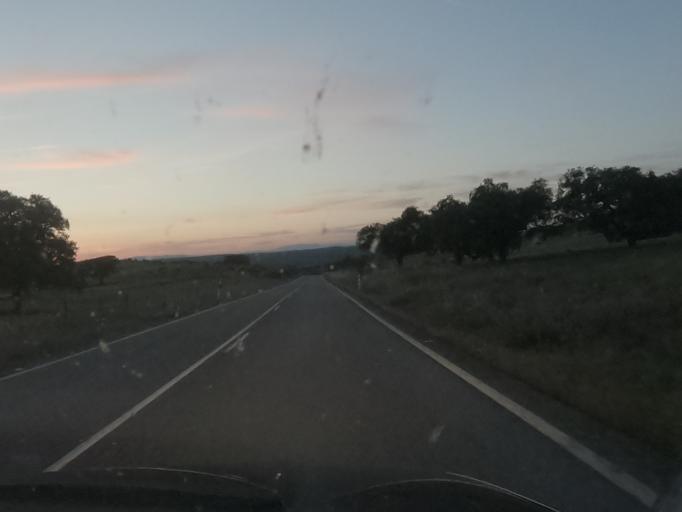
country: ES
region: Extremadura
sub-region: Provincia de Caceres
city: Piedras Albas
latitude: 39.7942
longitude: -6.9606
